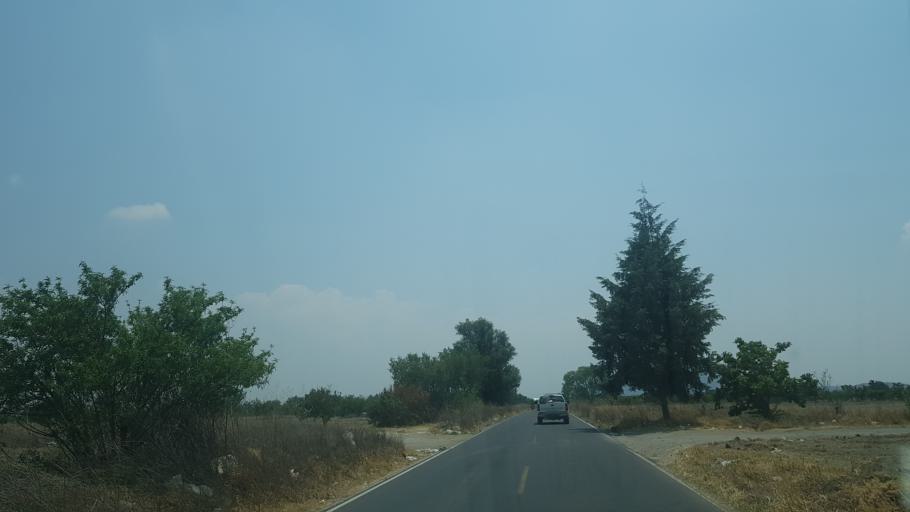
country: MX
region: Puebla
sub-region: San Jeronimo Tecuanipan
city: San Miguel Papaxtla
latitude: 19.0933
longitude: -98.3969
